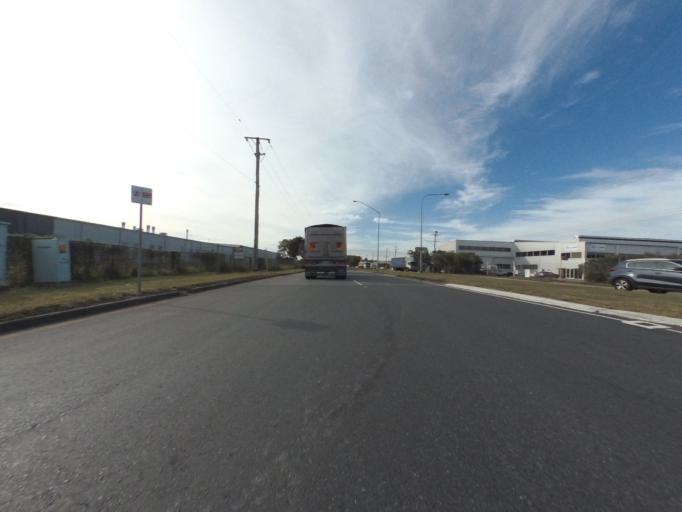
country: AU
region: Queensland
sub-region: Brisbane
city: Cannon Hill
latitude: -27.4291
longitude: 153.1033
